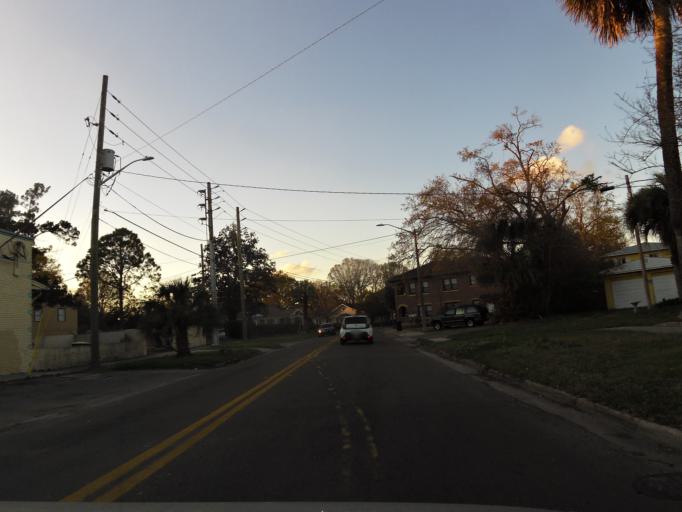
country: US
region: Florida
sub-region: Duval County
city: Jacksonville
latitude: 30.3143
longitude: -81.6964
